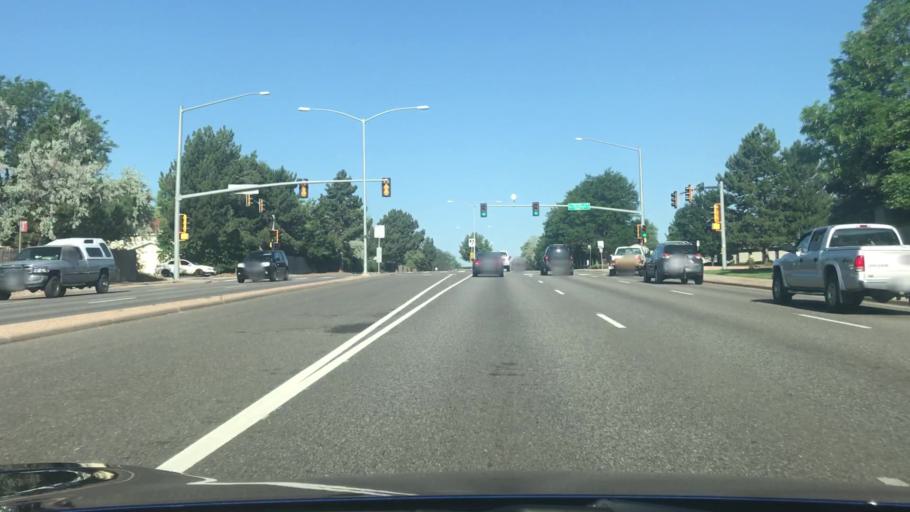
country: US
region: Colorado
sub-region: Arapahoe County
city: Dove Valley
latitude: 39.6531
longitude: -104.7837
